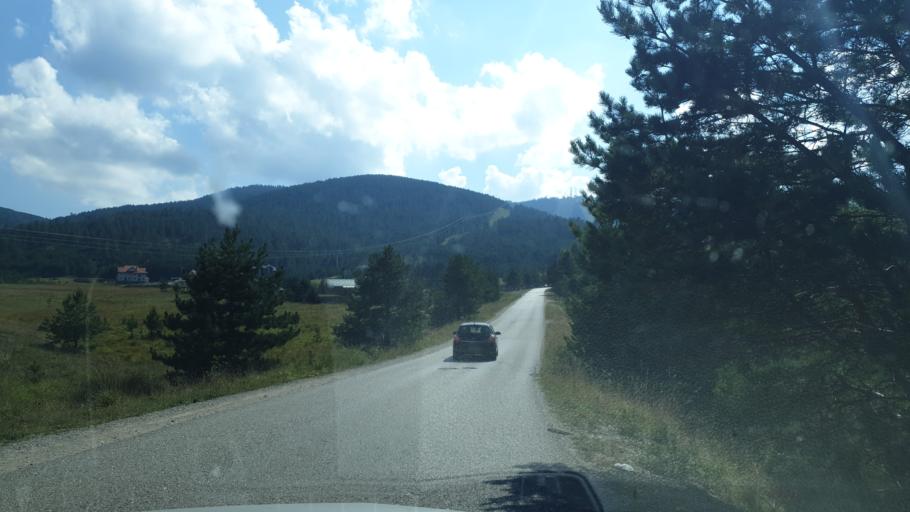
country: RS
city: Zlatibor
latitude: 43.6765
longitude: 19.6554
